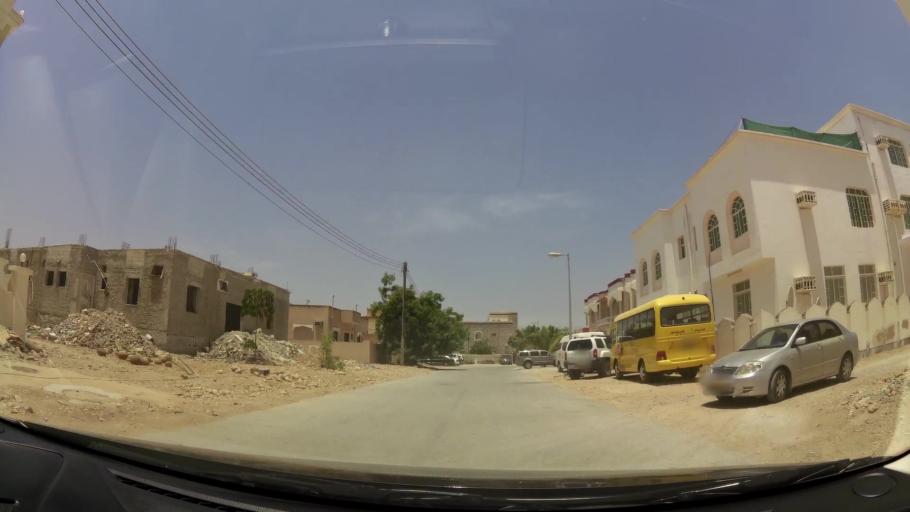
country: OM
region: Zufar
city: Salalah
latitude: 17.0720
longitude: 54.1548
